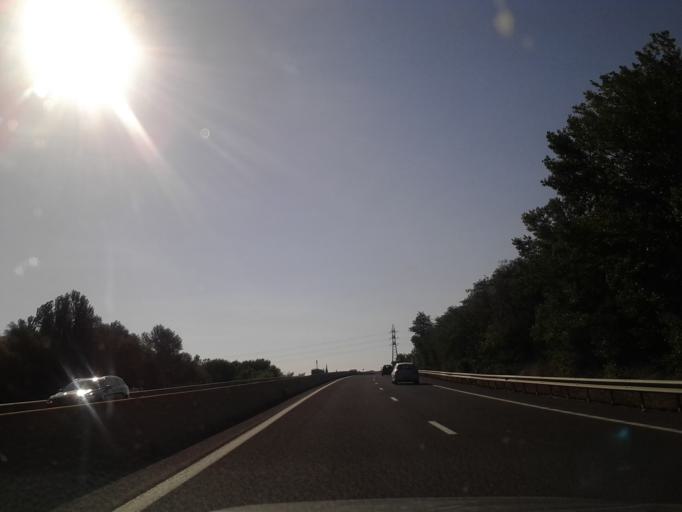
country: FR
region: Languedoc-Roussillon
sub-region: Departement des Pyrenees-Orientales
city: Pezilla-la-Riviere
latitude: 42.6827
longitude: 2.7727
